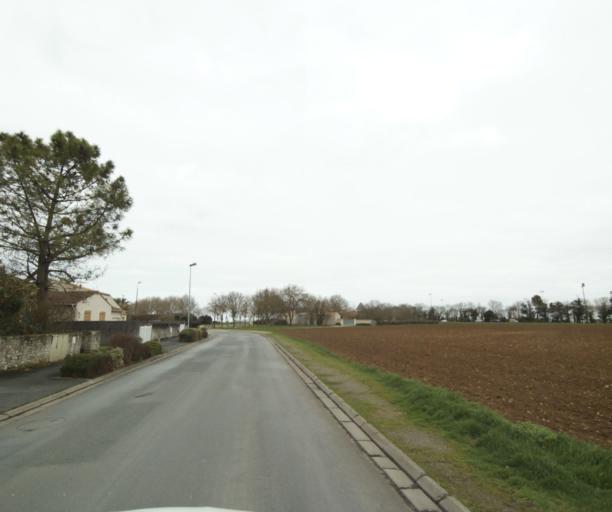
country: FR
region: Poitou-Charentes
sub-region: Departement de la Charente-Maritime
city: Lagord
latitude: 46.1936
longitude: -1.1554
